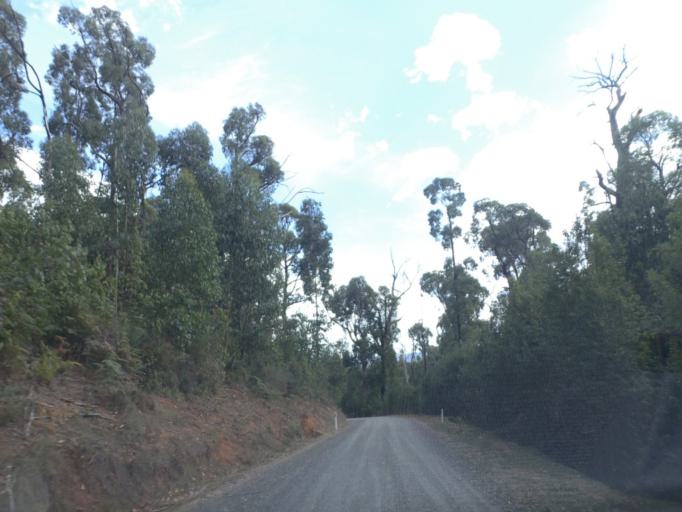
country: AU
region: Victoria
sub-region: Murrindindi
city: Alexandra
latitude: -37.4338
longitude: 145.7600
